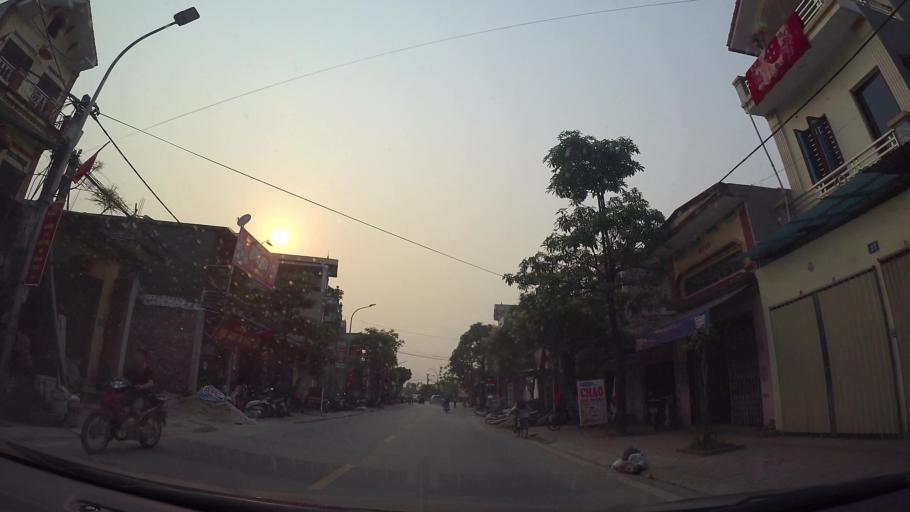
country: VN
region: Ha Noi
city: Thuong Tin
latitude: 20.8701
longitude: 105.8276
